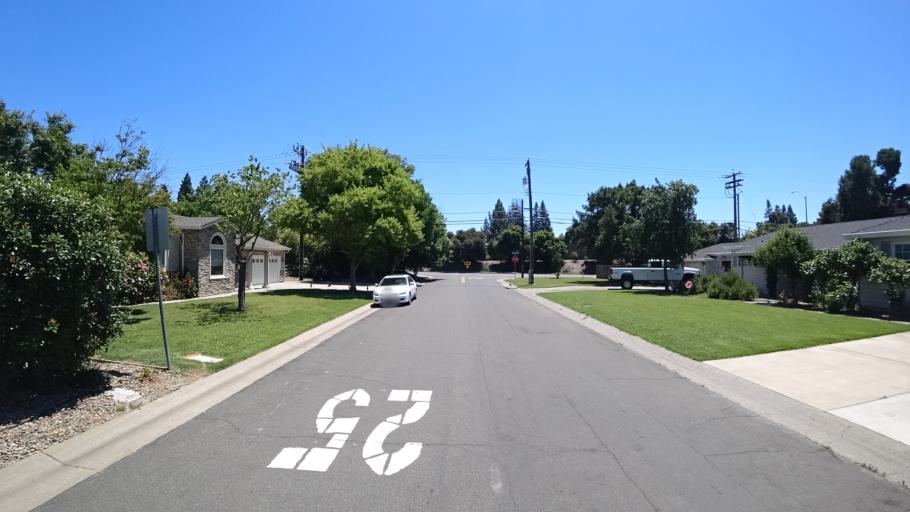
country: US
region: California
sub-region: Yolo County
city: West Sacramento
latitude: 38.5281
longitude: -121.5208
